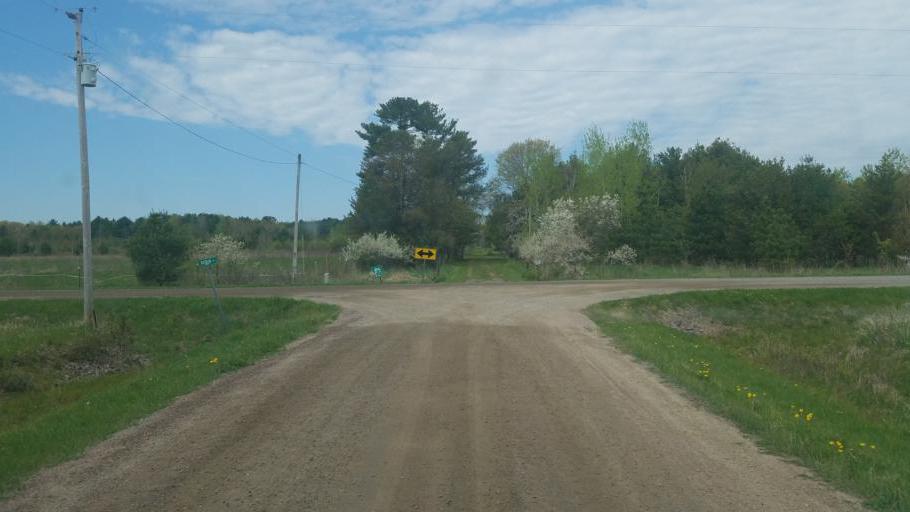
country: US
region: Wisconsin
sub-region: Clark County
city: Neillsville
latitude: 44.4733
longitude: -90.4661
